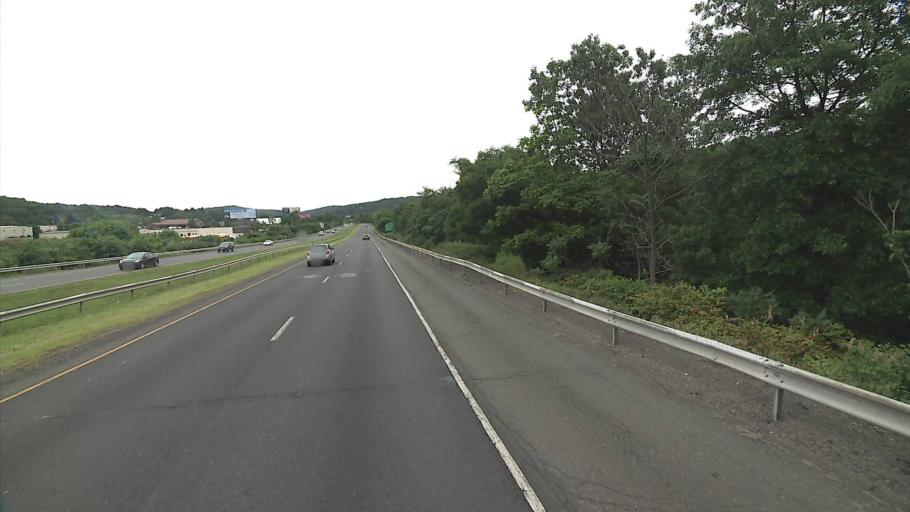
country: US
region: Connecticut
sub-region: New Haven County
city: Waterbury
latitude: 41.5711
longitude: -73.0553
